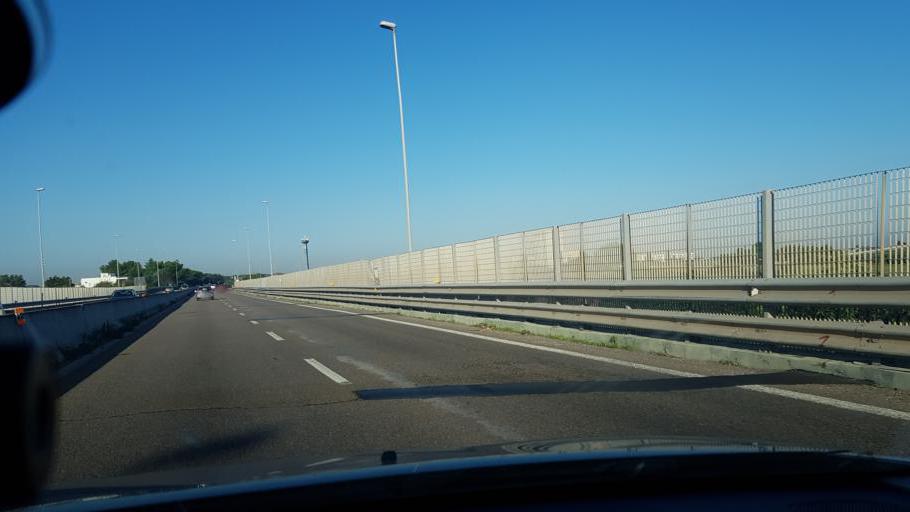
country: IT
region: Apulia
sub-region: Provincia di Bari
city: Triggiano
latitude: 41.0928
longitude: 16.9544
